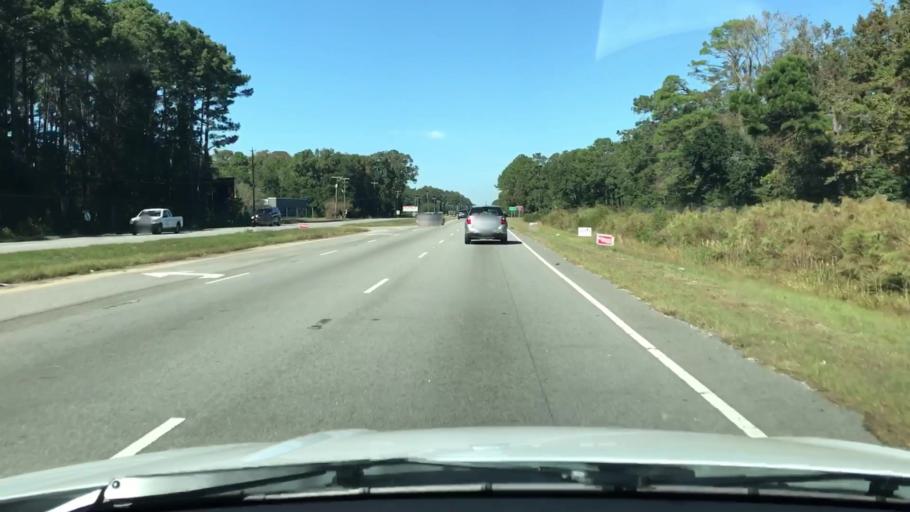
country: US
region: South Carolina
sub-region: Beaufort County
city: Burton
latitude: 32.4758
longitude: -80.7378
